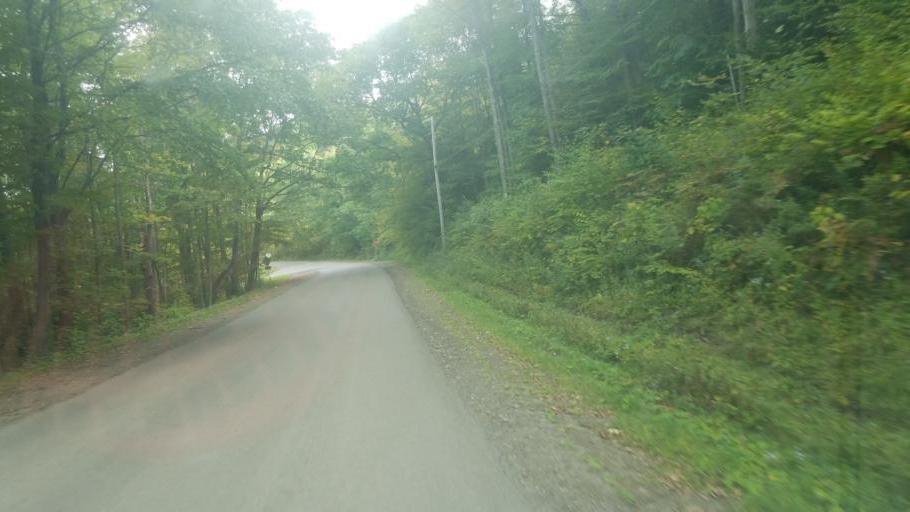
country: US
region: New York
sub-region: Cattaraugus County
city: Weston Mills
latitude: 42.1580
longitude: -78.3627
